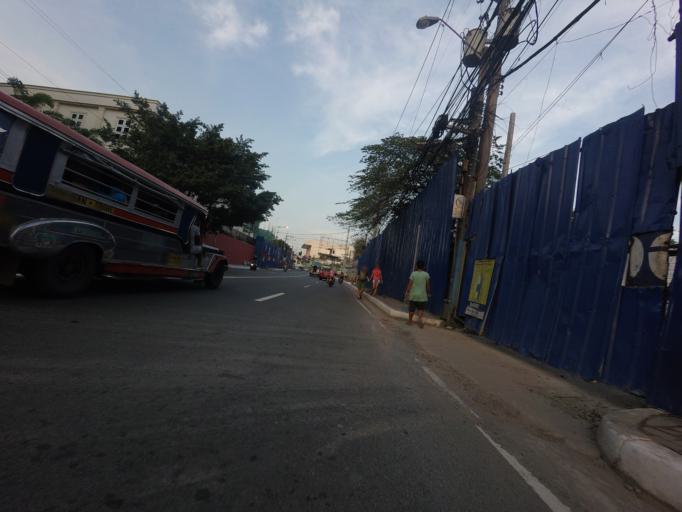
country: PH
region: Metro Manila
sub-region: San Juan
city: San Juan
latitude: 14.6040
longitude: 121.0316
